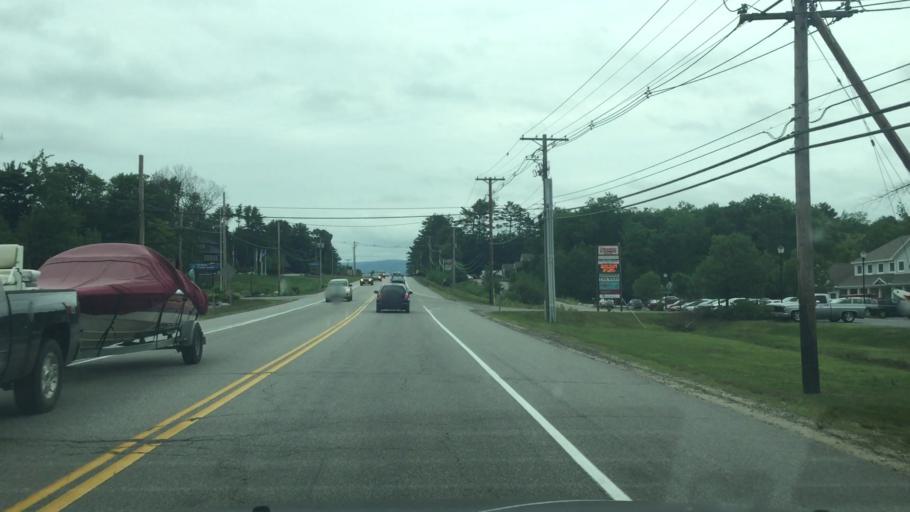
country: US
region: New Hampshire
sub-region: Carroll County
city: Center Harbor
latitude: 43.7122
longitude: -71.4541
